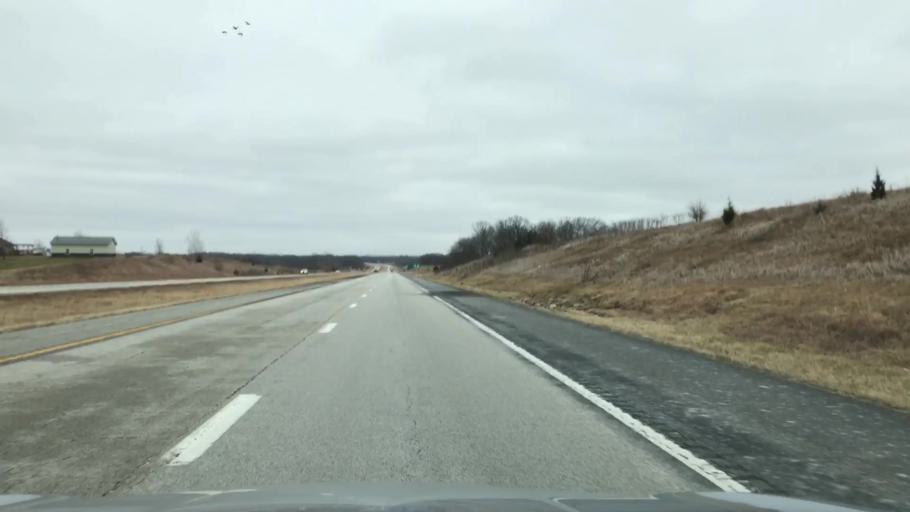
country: US
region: Missouri
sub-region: Caldwell County
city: Hamilton
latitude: 39.7454
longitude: -94.0453
